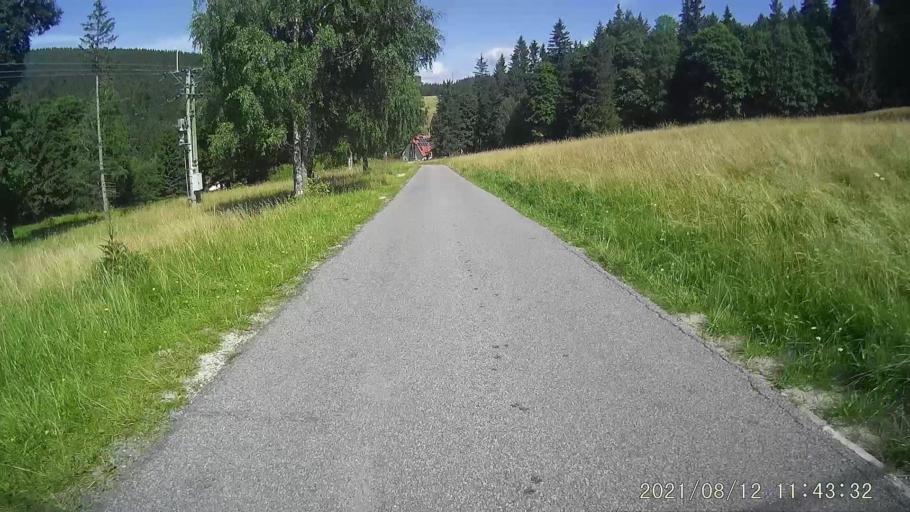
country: PL
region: Lower Silesian Voivodeship
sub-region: Powiat klodzki
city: Stronie Slaskie
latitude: 50.2622
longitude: 16.8342
